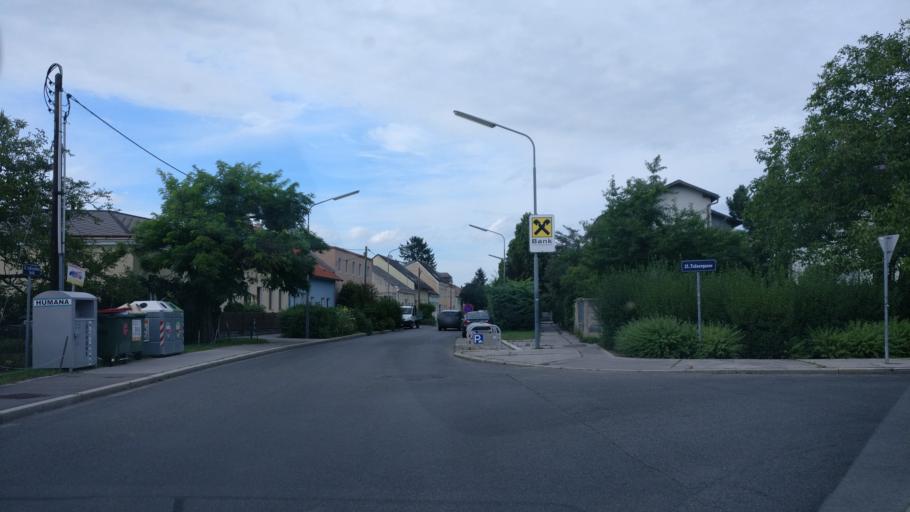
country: AT
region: Lower Austria
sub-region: Politischer Bezirk Korneuburg
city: Hagenbrunn
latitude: 48.2905
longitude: 16.4111
